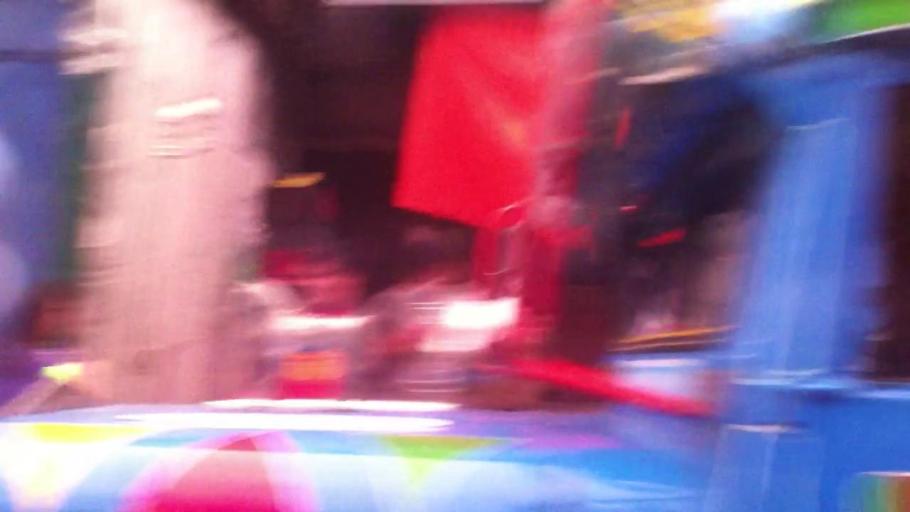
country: PH
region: Cordillera
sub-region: Province of Benguet
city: La Trinidad
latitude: 16.4421
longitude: 120.5929
